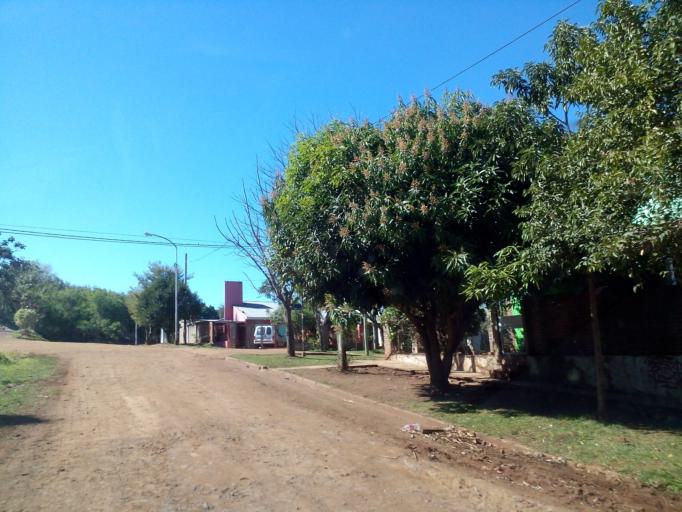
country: AR
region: Misiones
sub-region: Departamento de Capital
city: Posadas
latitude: -27.3899
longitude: -55.9407
